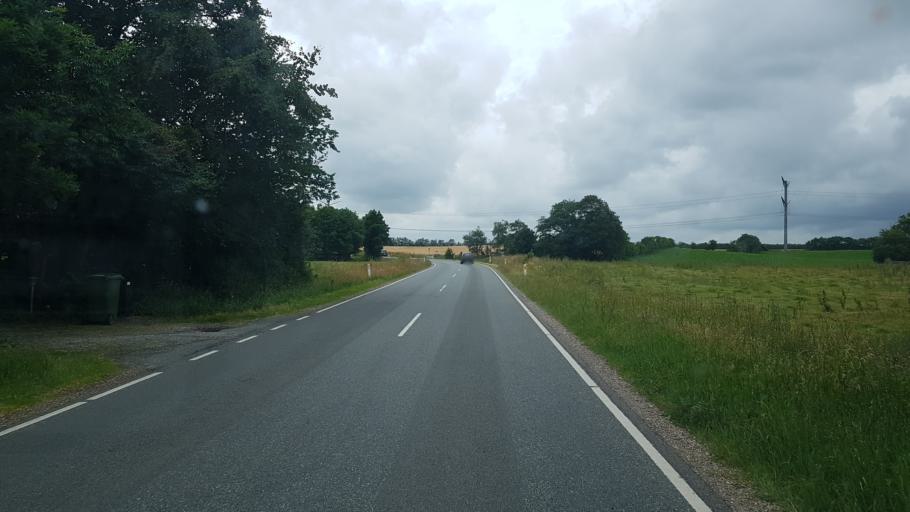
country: DK
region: South Denmark
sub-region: Vejen Kommune
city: Vejen
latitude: 55.4363
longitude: 9.1830
